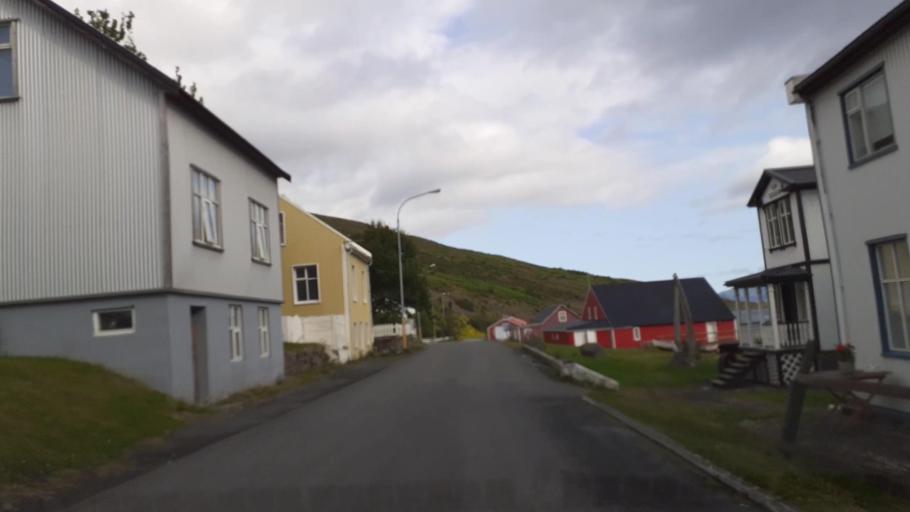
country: IS
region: East
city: Eskifjoerdur
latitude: 65.0648
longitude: -14.0003
